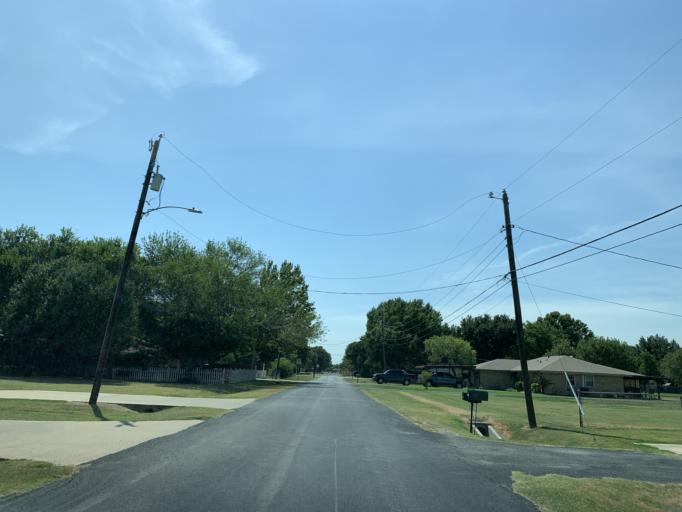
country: US
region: Texas
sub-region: Dallas County
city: Cedar Hill
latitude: 32.6503
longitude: -97.0195
